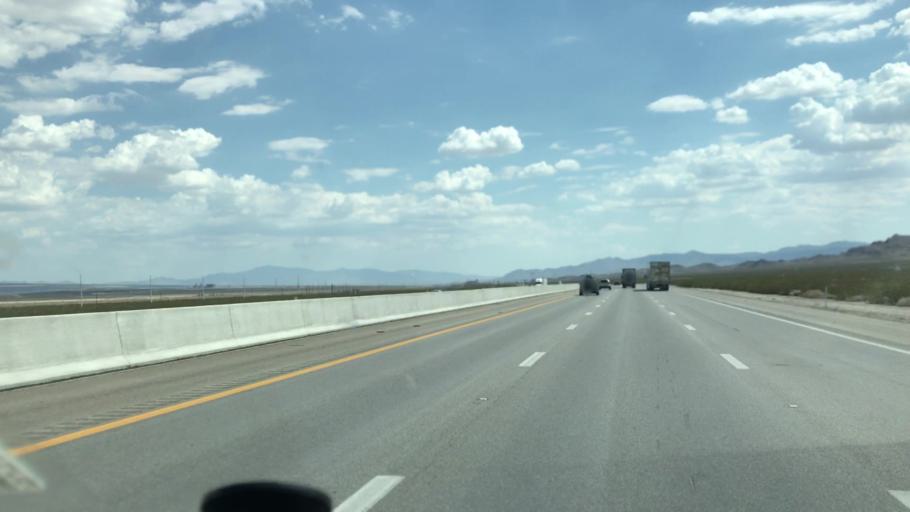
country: US
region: Nevada
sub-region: Clark County
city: Sandy Valley
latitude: 35.6886
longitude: -115.3749
